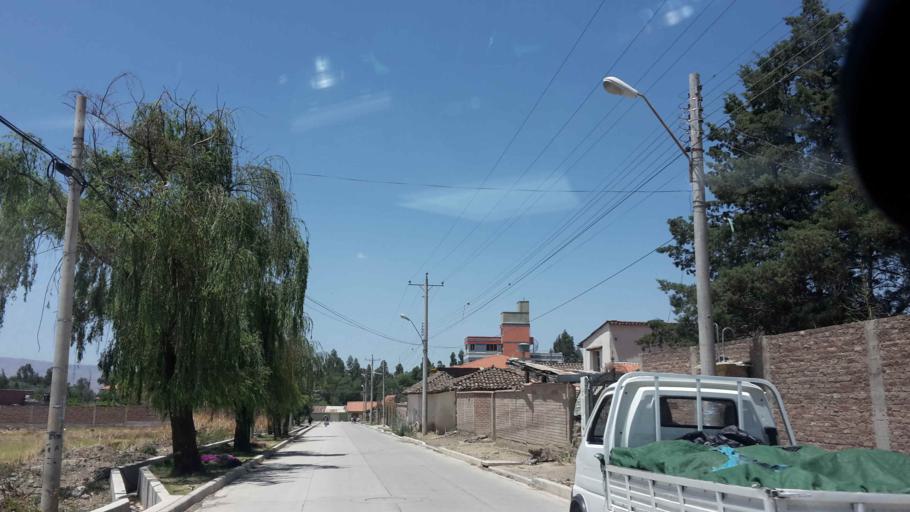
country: BO
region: Cochabamba
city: Cochabamba
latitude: -17.3544
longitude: -66.2072
